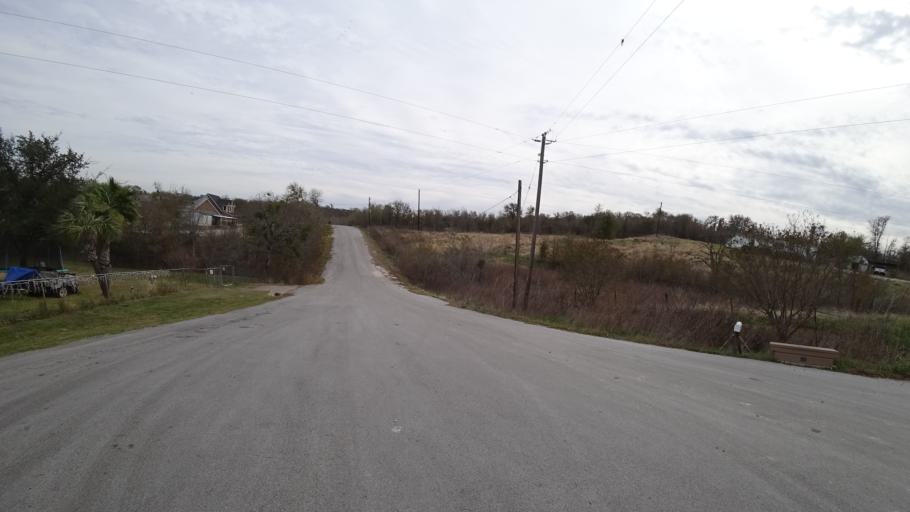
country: US
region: Texas
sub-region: Travis County
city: Garfield
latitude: 30.1474
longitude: -97.5884
